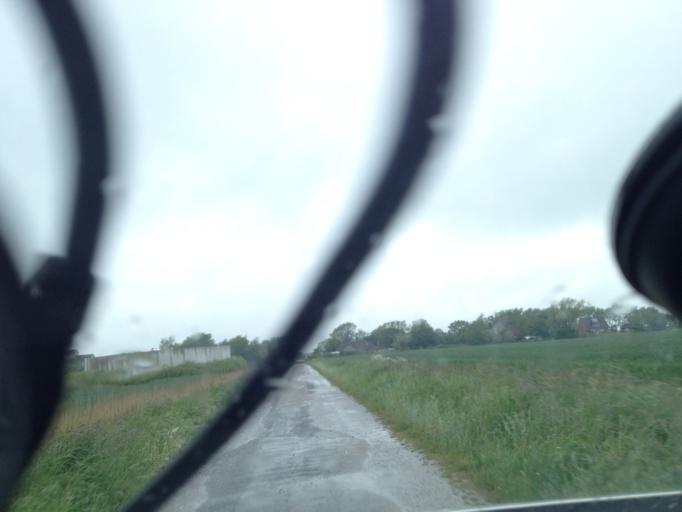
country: DE
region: Schleswig-Holstein
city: Klanxbull
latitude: 54.8851
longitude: 8.6913
